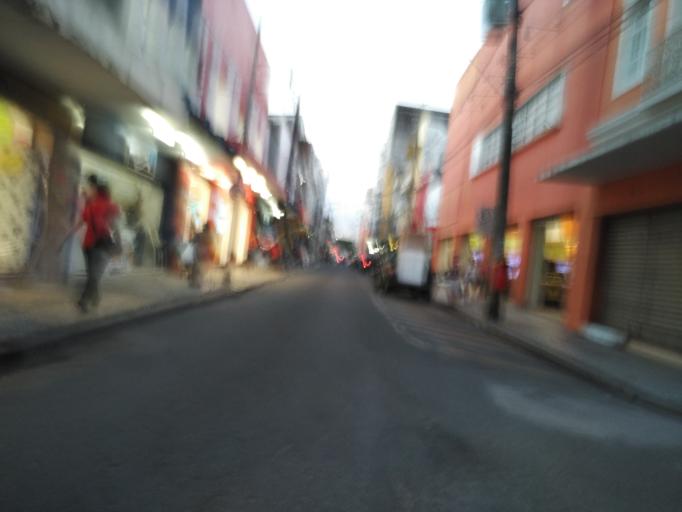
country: BR
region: Pernambuco
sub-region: Recife
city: Recife
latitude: -8.0661
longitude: -34.8815
